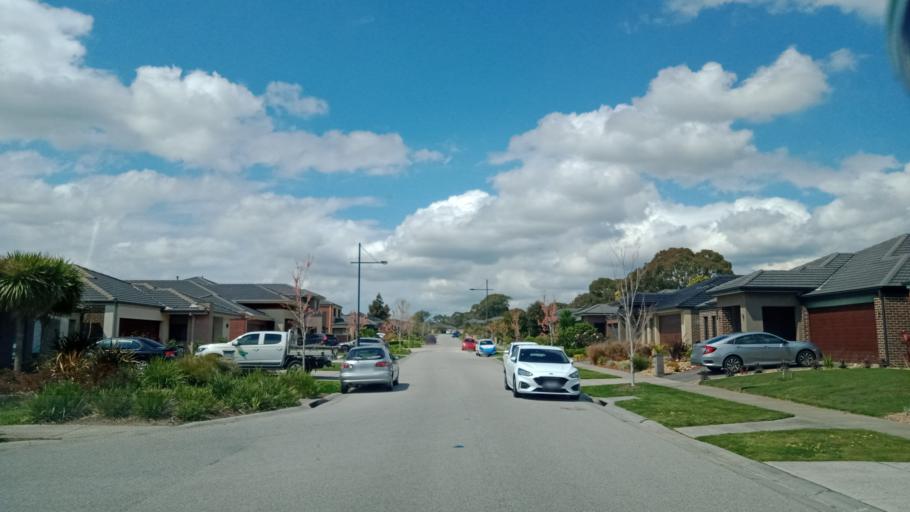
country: AU
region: Victoria
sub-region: Frankston
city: Sandhurst
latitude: -38.0868
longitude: 145.1940
